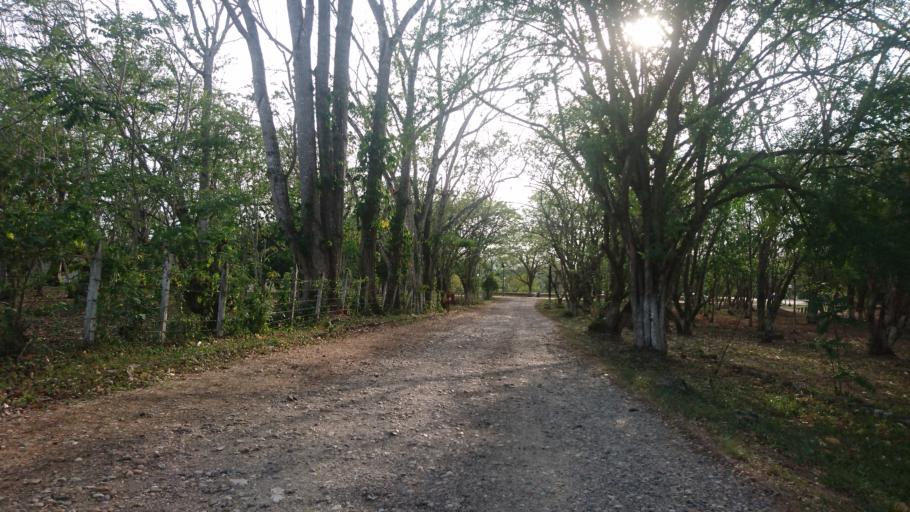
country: MX
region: Chiapas
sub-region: Ocosingo
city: Frontera Corozal
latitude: 16.8228
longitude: -90.8860
